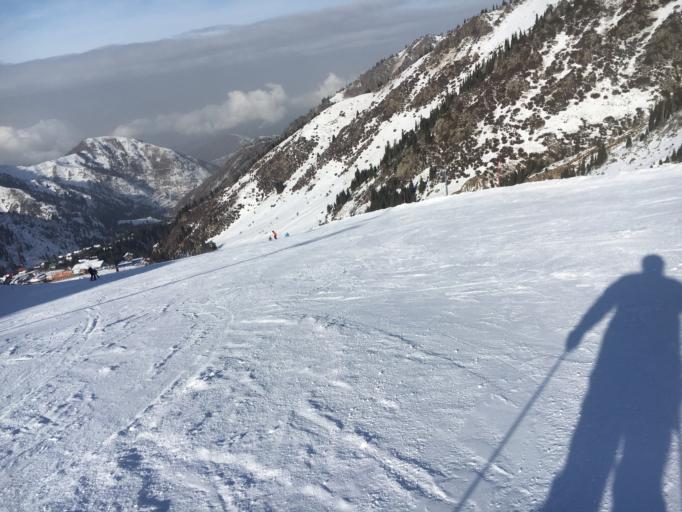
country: KZ
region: Almaty Qalasy
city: Almaty
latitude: 43.1223
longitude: 77.0944
